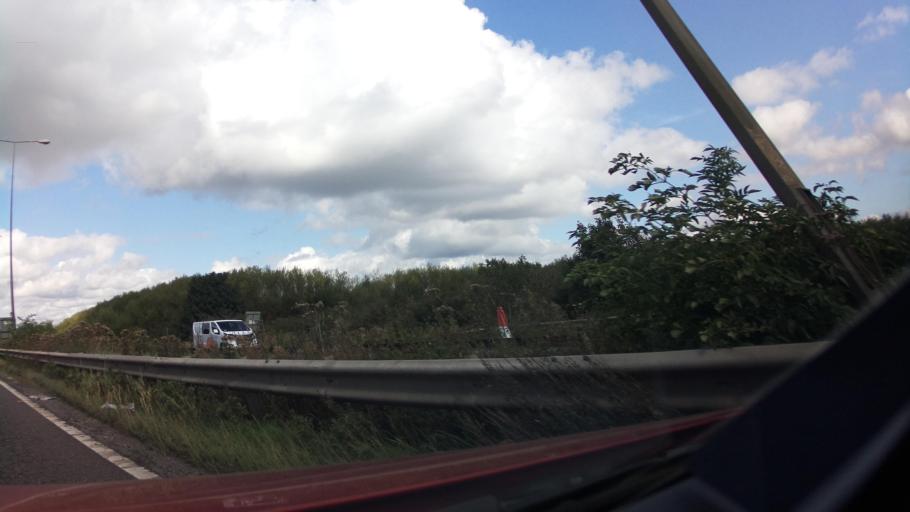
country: GB
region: England
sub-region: Borough of Wigan
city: Shevington
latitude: 53.5499
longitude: -2.7003
